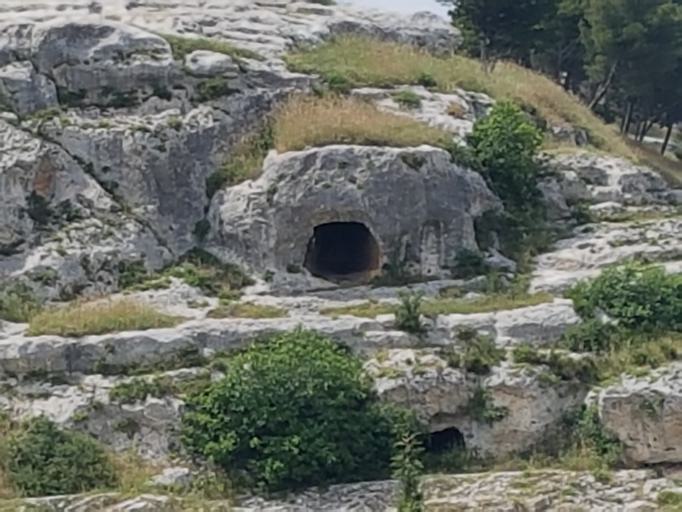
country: IT
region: Apulia
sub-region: Provincia di Bari
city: Gravina in Puglia
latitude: 40.8200
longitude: 16.4139
